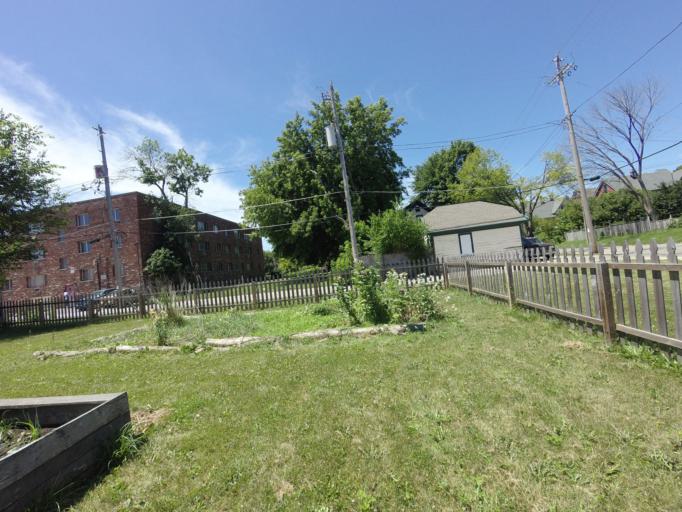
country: US
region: Wisconsin
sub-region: Milwaukee County
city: West Milwaukee
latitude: 43.0425
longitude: -87.9481
